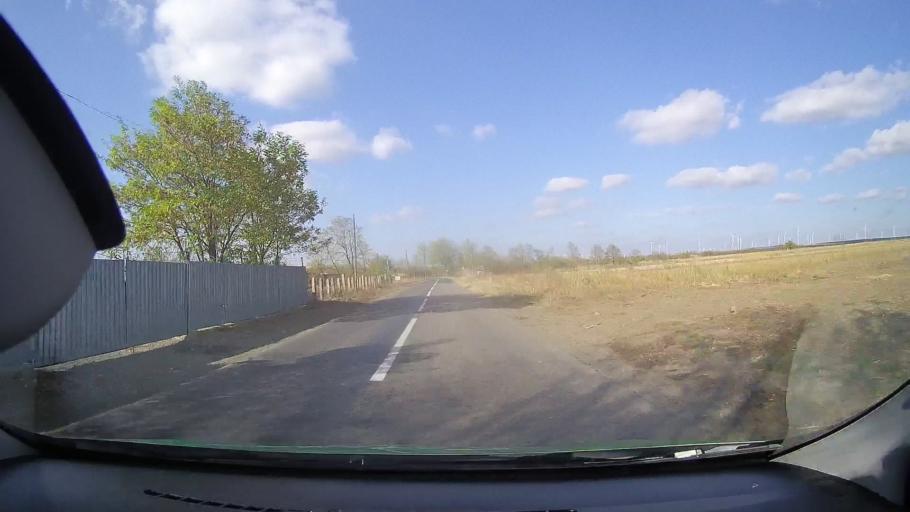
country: RO
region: Constanta
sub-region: Comuna Cogealac
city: Tariverde
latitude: 44.5626
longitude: 28.6059
